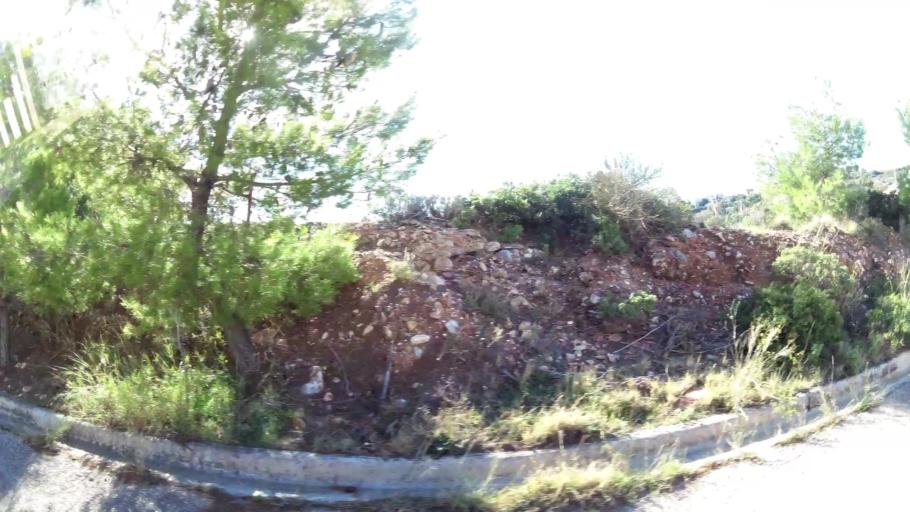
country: GR
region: Attica
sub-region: Nomarchia Anatolikis Attikis
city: Dhrafi
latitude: 38.0274
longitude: 23.9040
